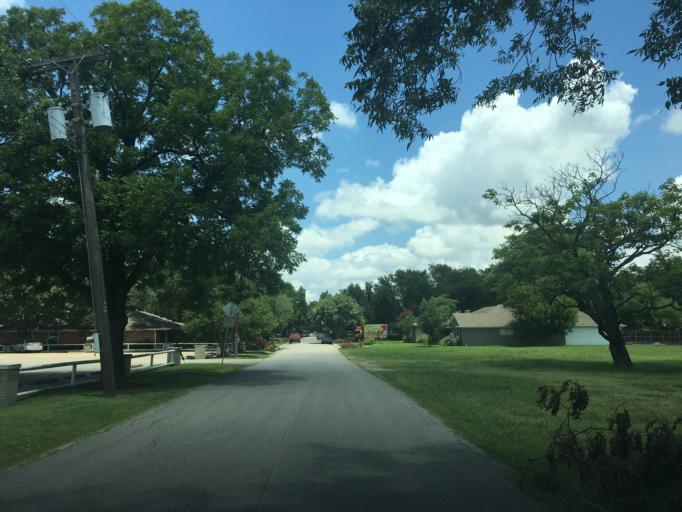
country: US
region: Texas
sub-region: Dallas County
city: Highland Park
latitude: 32.8555
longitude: -96.7413
